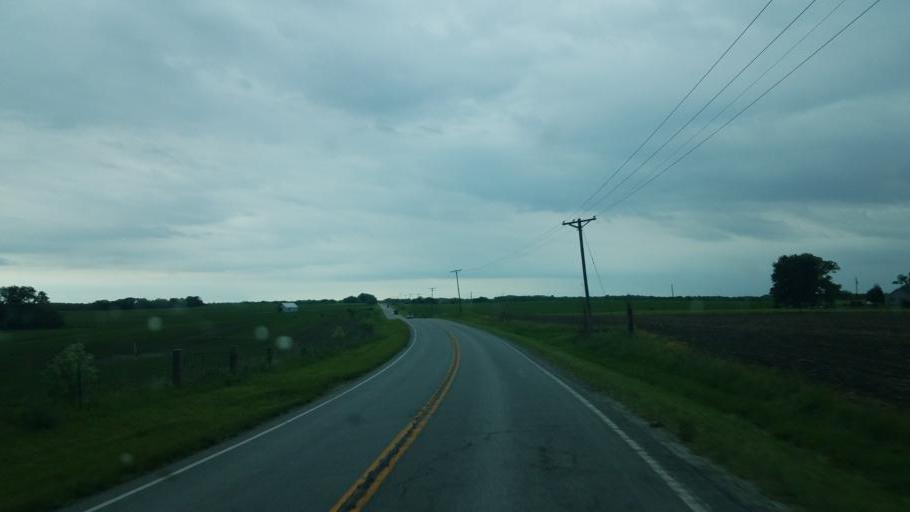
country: US
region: Missouri
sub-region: Cooper County
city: Boonville
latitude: 38.8519
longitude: -92.6347
